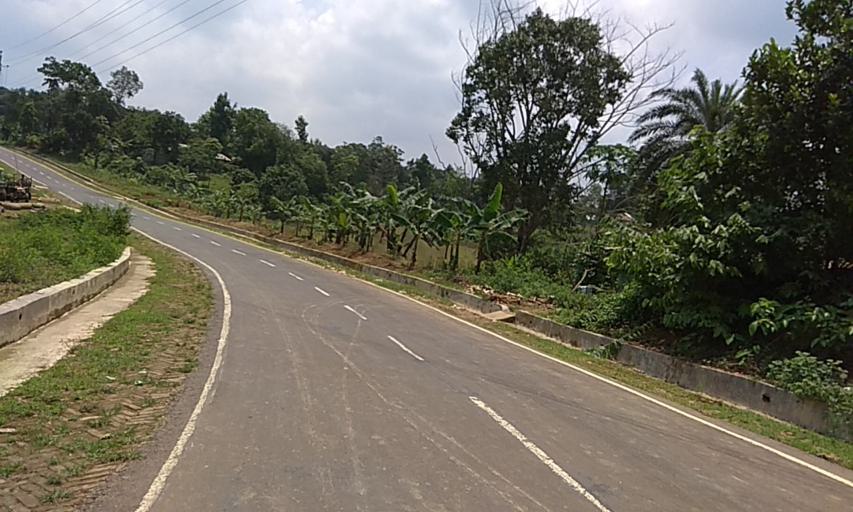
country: BD
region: Chittagong
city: Manikchari
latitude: 22.9354
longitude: 91.8955
